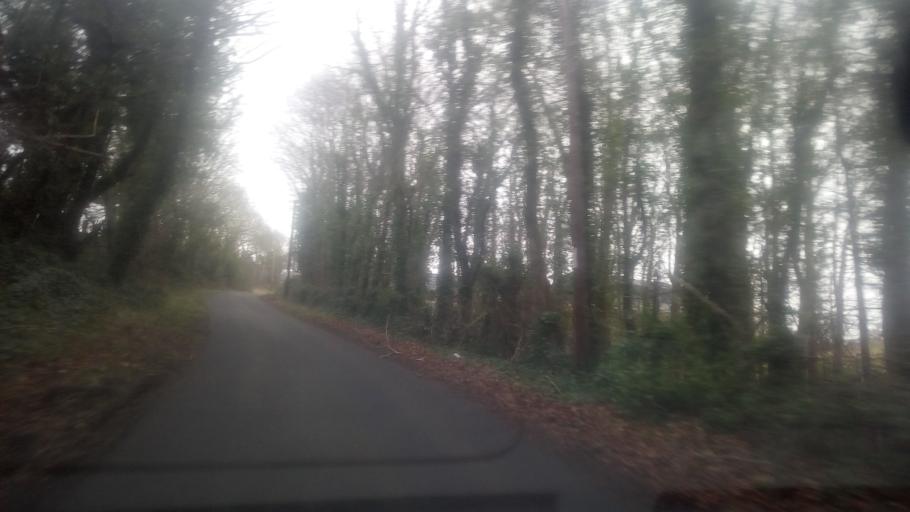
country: GB
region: Scotland
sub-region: The Scottish Borders
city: Kelso
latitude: 55.5735
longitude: -2.5171
